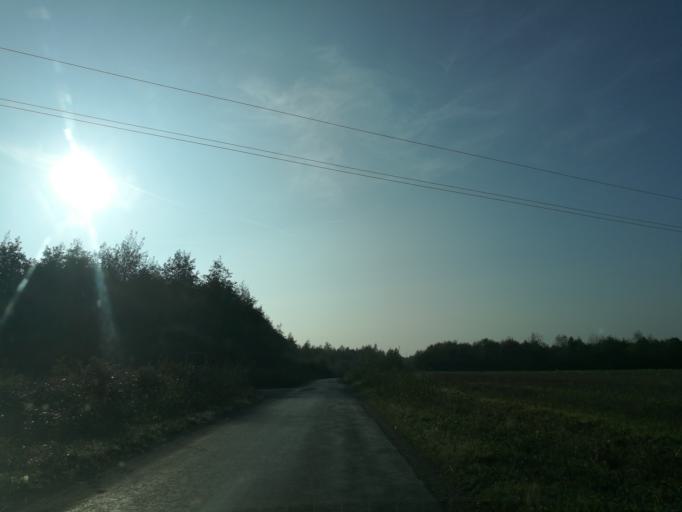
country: FR
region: Brittany
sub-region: Departement d'Ille-et-Vilaine
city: Pleumeleuc
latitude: 48.1725
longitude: -1.8991
